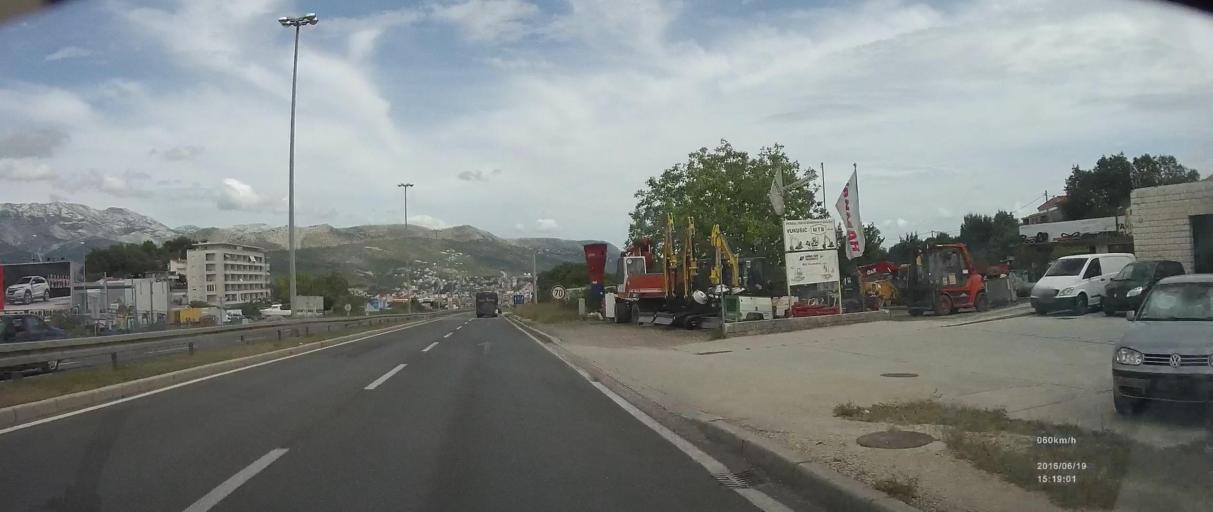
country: HR
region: Splitsko-Dalmatinska
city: Kamen
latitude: 43.5078
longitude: 16.5003
